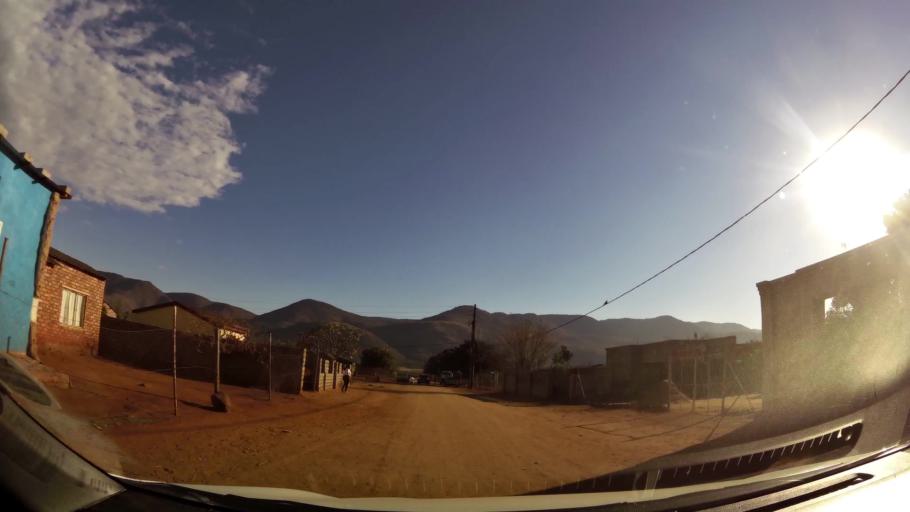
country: ZA
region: Limpopo
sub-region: Waterberg District Municipality
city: Mokopane
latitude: -24.1845
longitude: 28.9718
